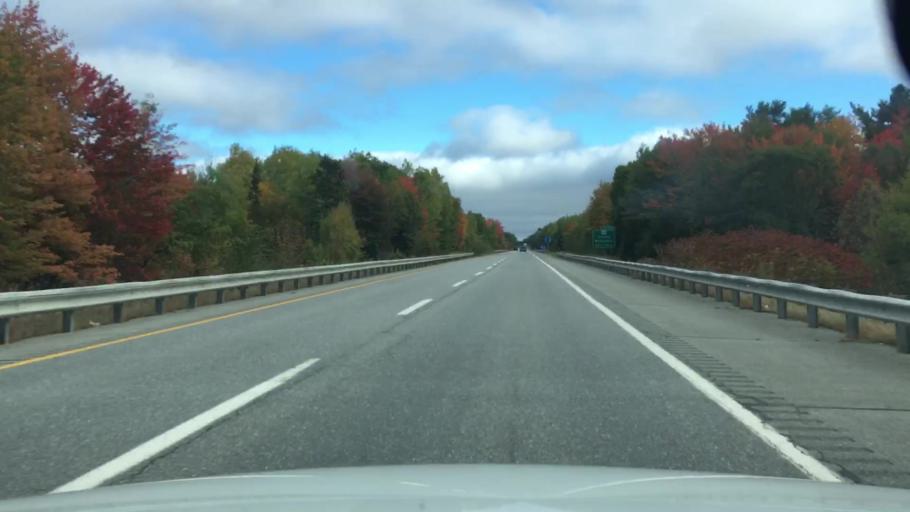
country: US
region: Maine
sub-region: Penobscot County
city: Carmel
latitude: 44.7681
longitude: -68.9978
